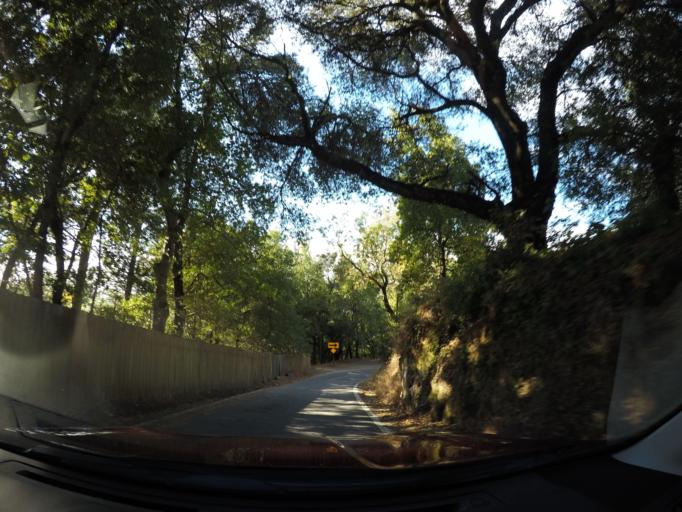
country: US
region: California
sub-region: Santa Clara County
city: Lexington Hills
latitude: 37.1628
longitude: -122.0134
